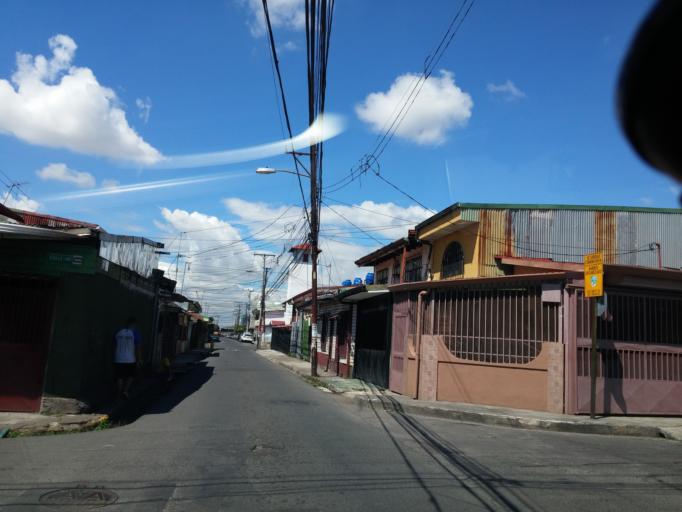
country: CR
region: San Jose
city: San Jose
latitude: 9.9240
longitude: -84.0890
